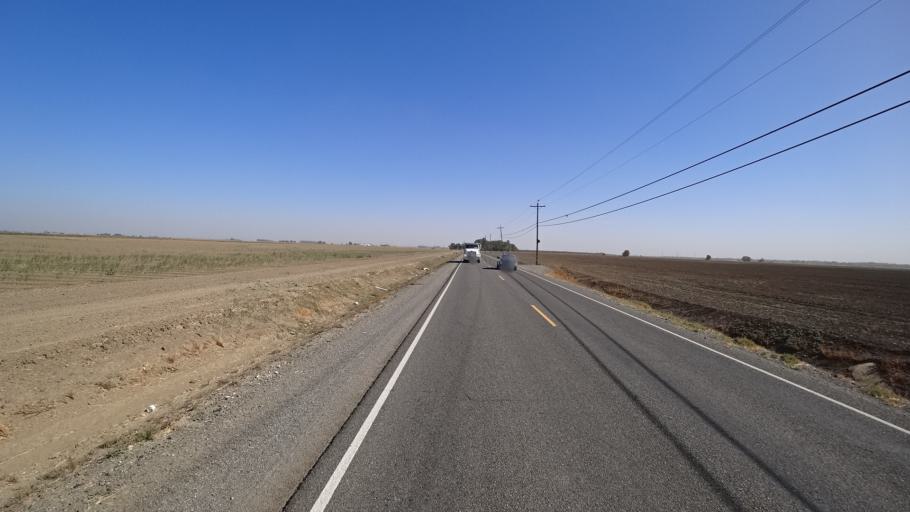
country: US
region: California
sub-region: Yolo County
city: Davis
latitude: 38.5900
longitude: -121.7490
